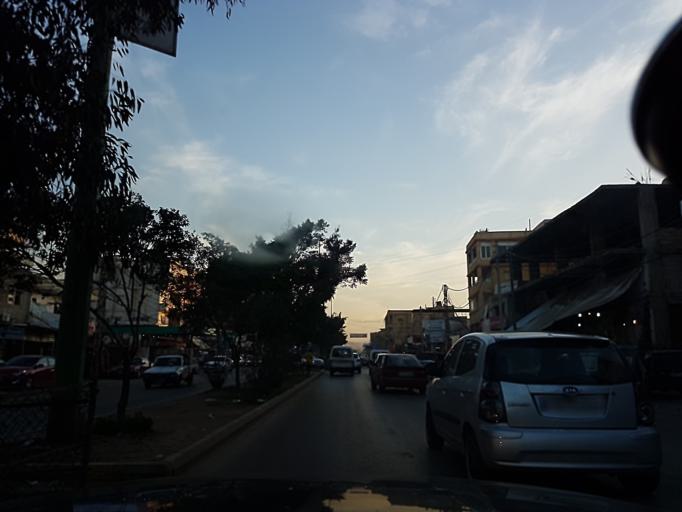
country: LB
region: Beyrouth
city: Beirut
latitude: 33.8357
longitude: 35.4846
